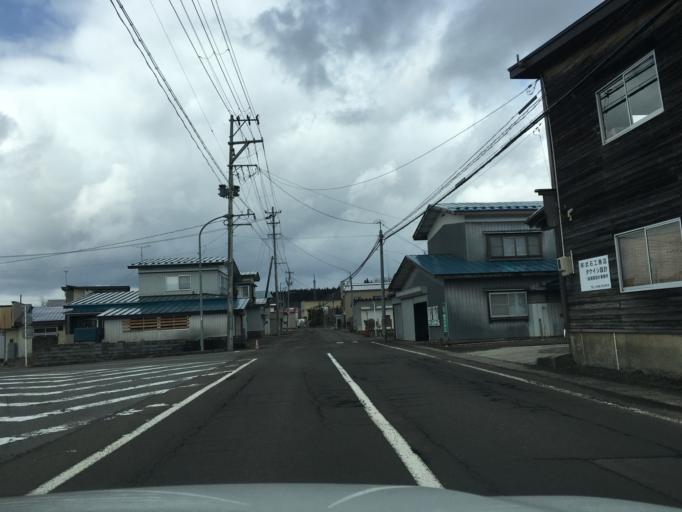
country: JP
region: Akita
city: Takanosu
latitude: 40.1578
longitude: 140.3333
